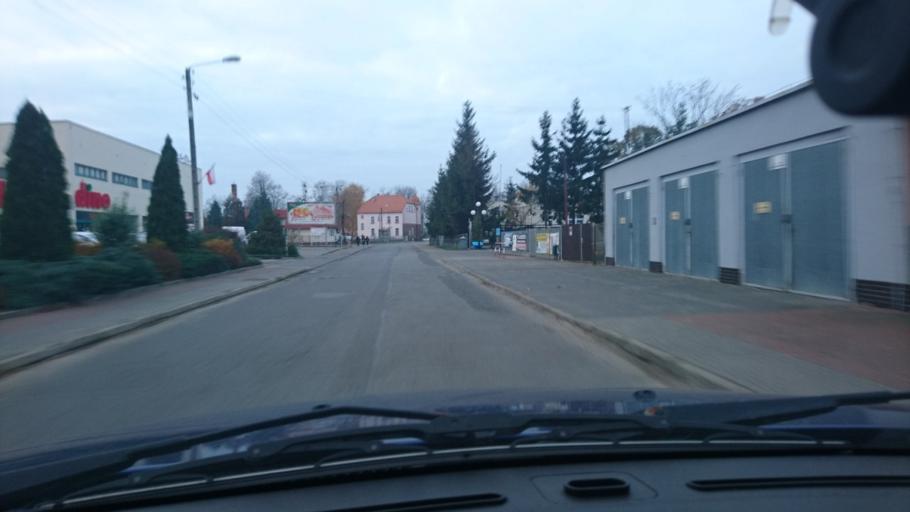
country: PL
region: Greater Poland Voivodeship
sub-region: Powiat ostrowski
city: Odolanow
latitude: 51.5730
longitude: 17.6724
